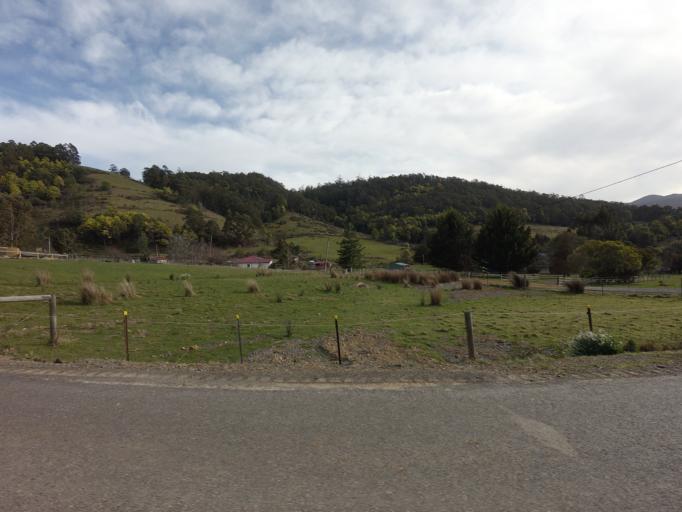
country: AU
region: Tasmania
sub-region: Kingborough
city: Margate
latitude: -42.9942
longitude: 147.1834
